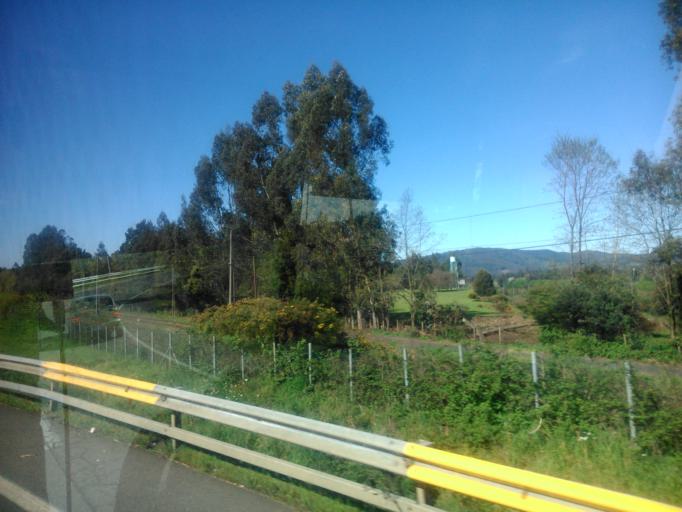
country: CL
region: Araucania
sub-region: Provincia de Cautin
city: Temuco
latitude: -38.7847
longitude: -72.6120
